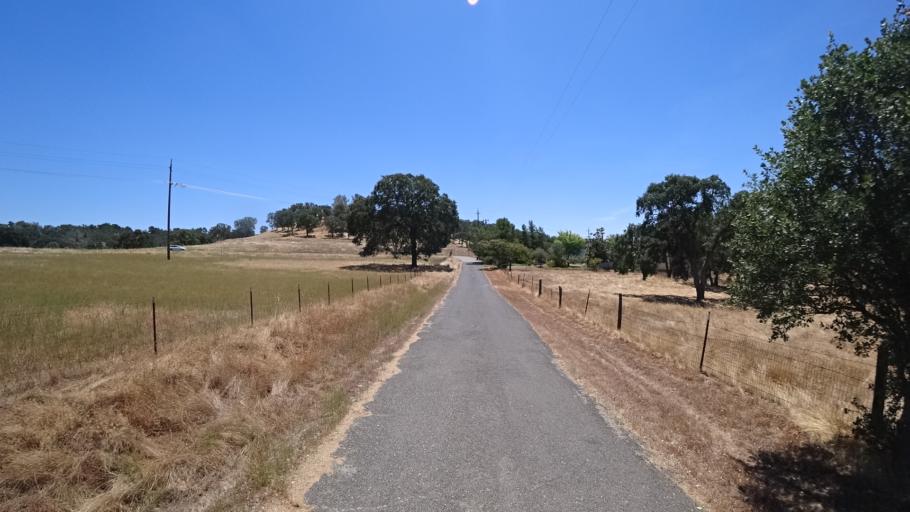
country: US
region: California
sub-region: Calaveras County
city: Rancho Calaveras
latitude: 38.1219
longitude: -120.8816
